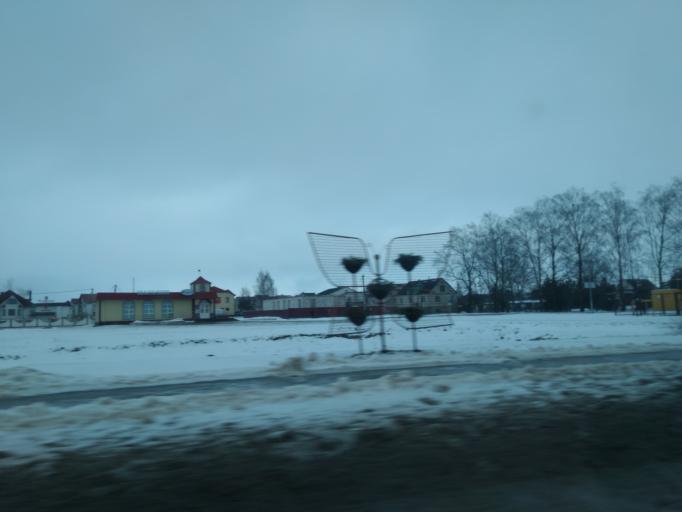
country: BY
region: Minsk
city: Nyasvizh
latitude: 53.2271
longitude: 26.6658
